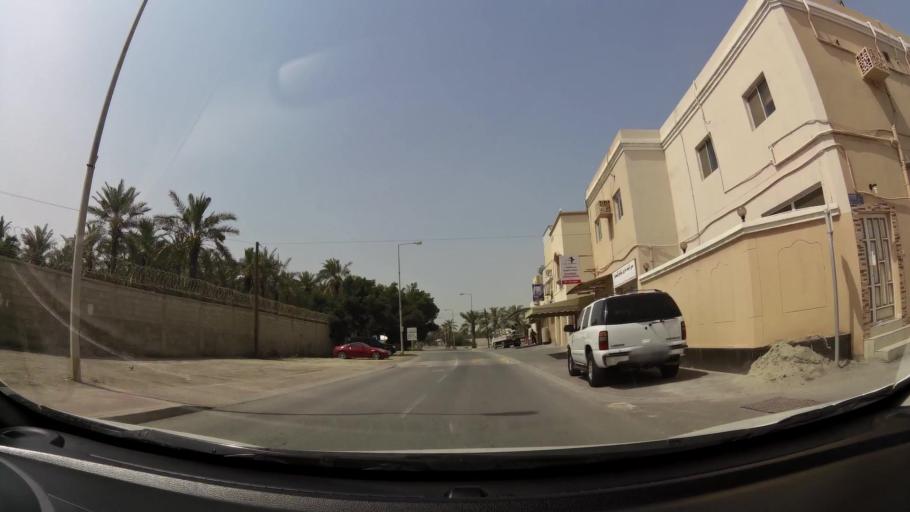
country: BH
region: Manama
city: Jidd Hafs
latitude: 26.2304
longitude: 50.4765
